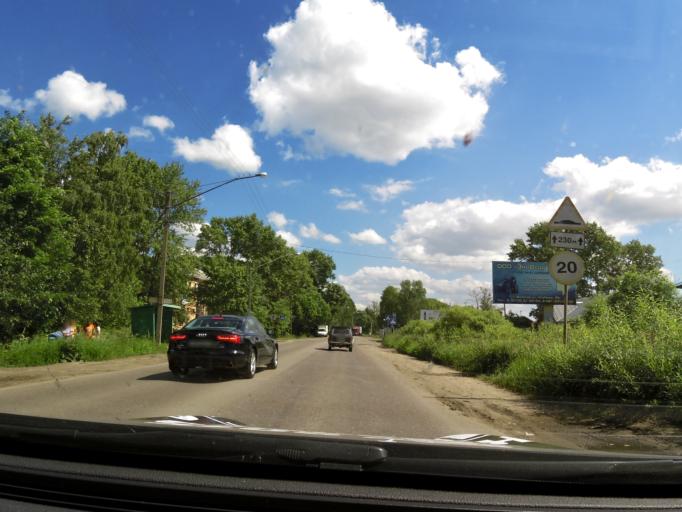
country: RU
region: Vologda
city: Vologda
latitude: 59.2384
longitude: 39.8081
